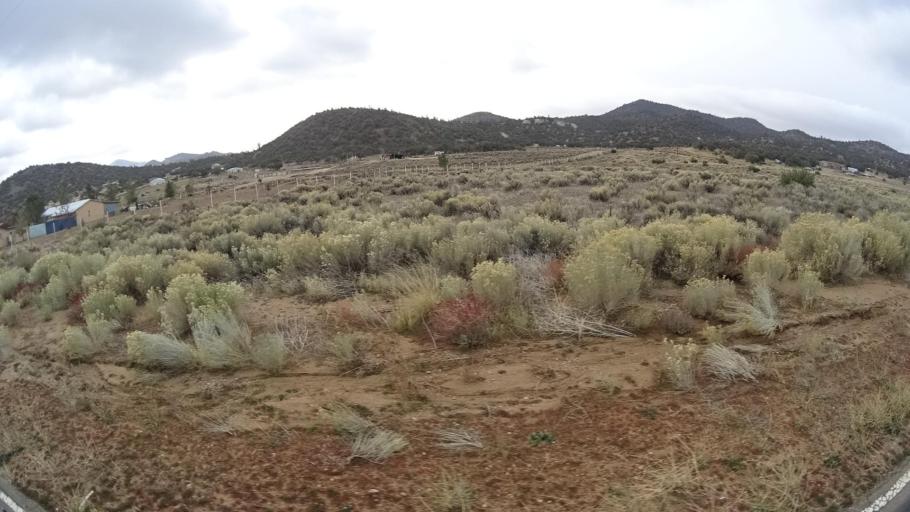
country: US
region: California
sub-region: Kern County
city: Tehachapi
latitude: 35.1746
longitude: -118.3516
